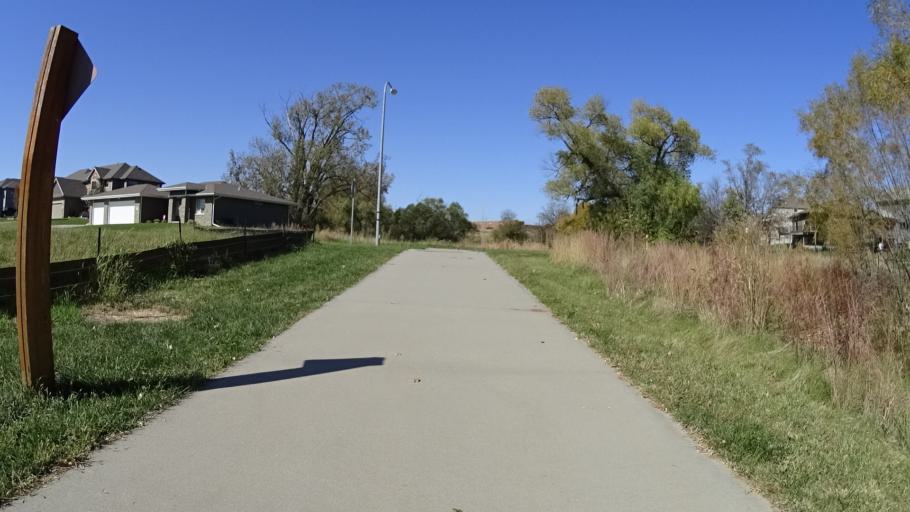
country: US
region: Nebraska
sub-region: Sarpy County
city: La Vista
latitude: 41.1668
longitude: -96.0158
